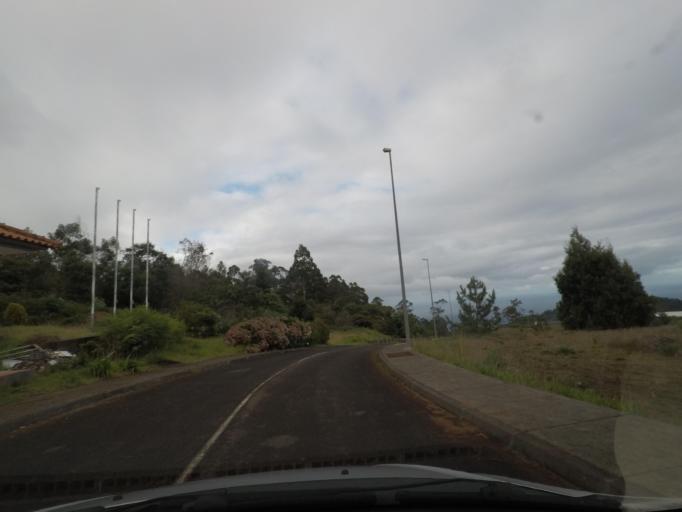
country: PT
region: Madeira
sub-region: Santana
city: Santana
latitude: 32.7861
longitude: -16.8803
